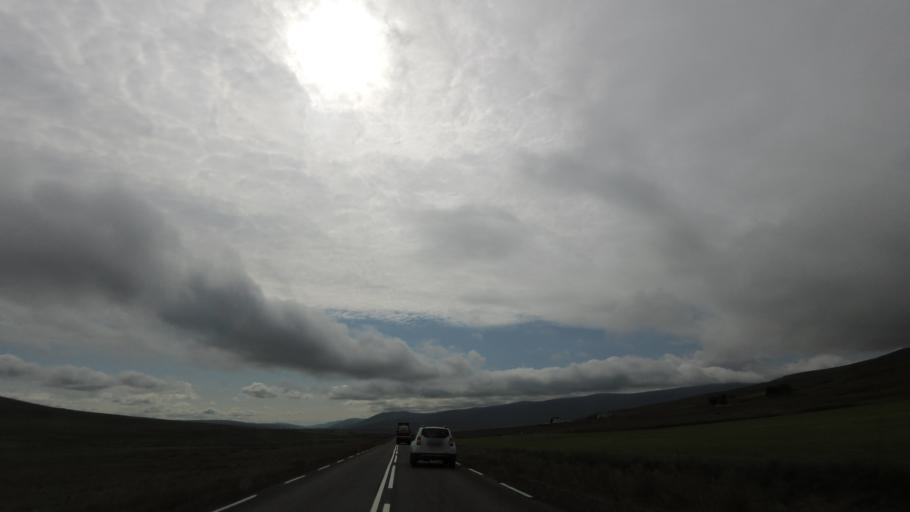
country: IS
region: Northeast
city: Laugar
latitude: 65.7395
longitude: -17.5915
